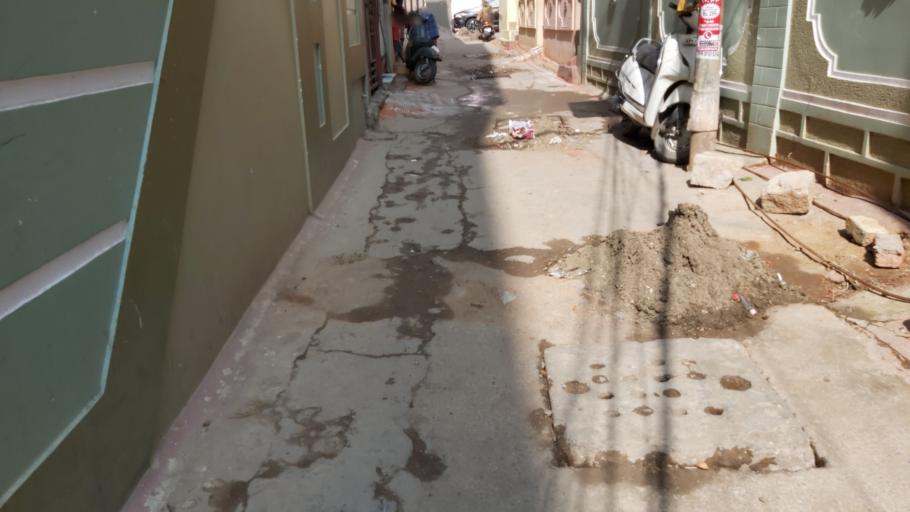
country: IN
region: Telangana
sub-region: Rangareddi
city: Gaddi Annaram
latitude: 17.3665
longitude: 78.5227
